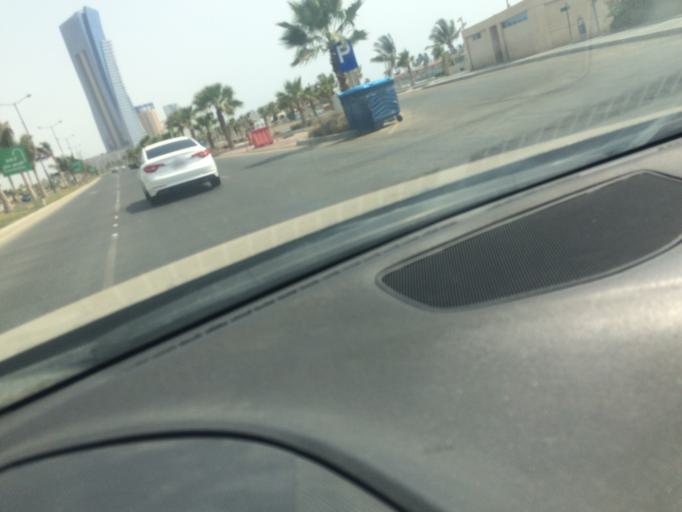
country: SA
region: Makkah
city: Jeddah
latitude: 21.5854
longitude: 39.1088
